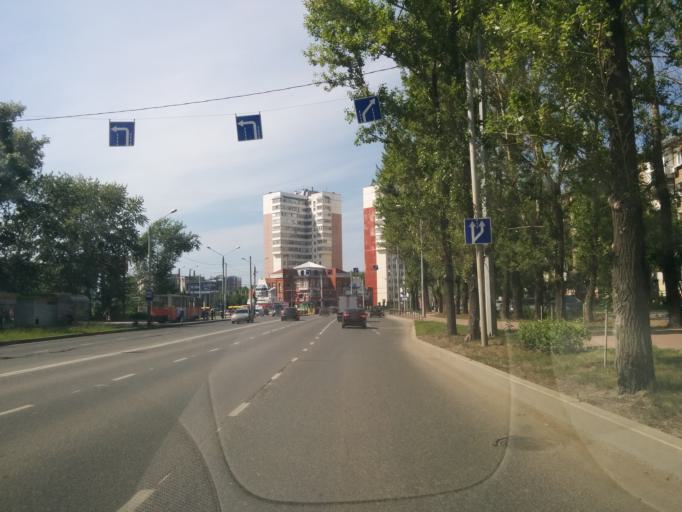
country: RU
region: Perm
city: Perm
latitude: 57.9939
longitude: 56.2895
